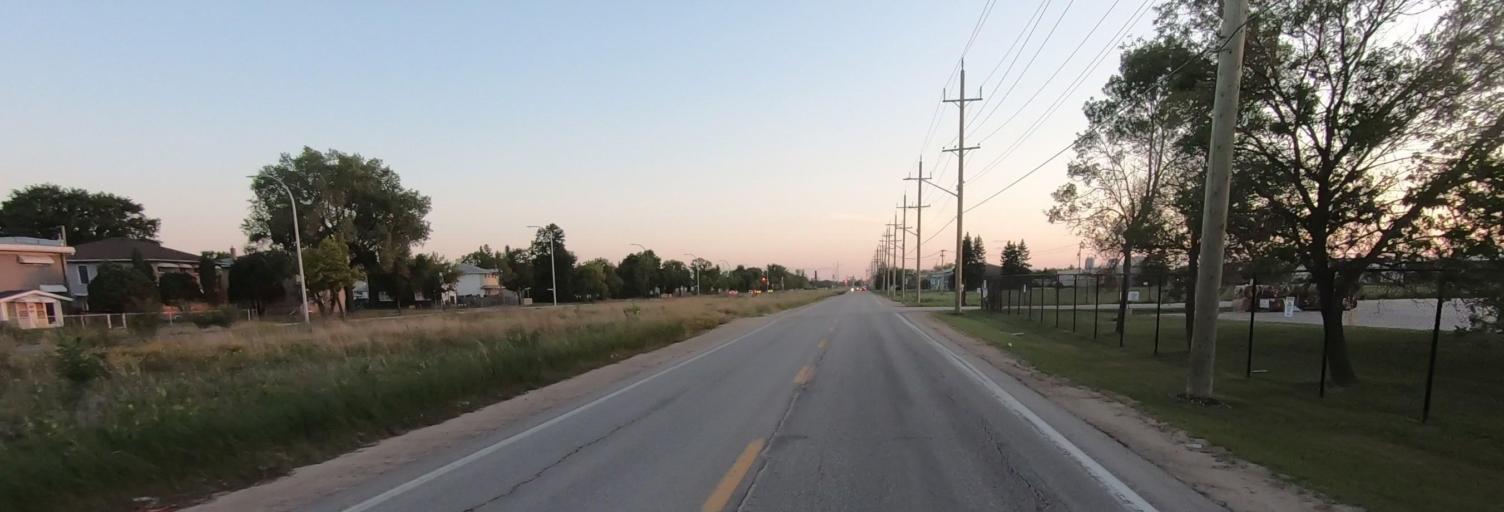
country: CA
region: Manitoba
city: Winnipeg
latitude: 49.9178
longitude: -97.0862
